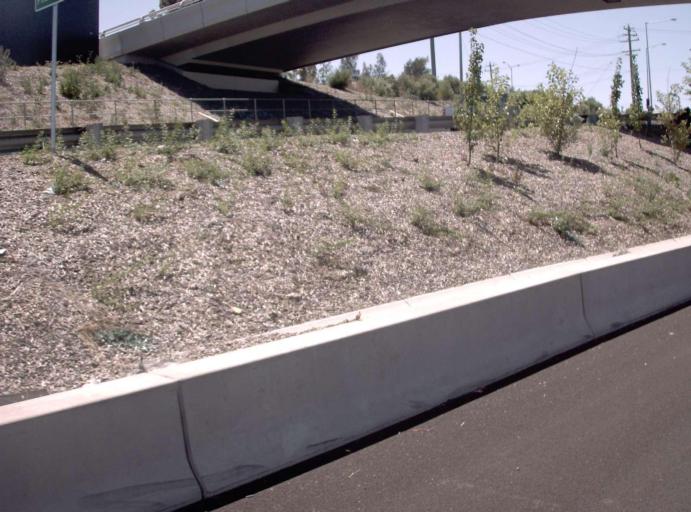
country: AU
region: Victoria
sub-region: Hume
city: Jacana
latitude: -37.6940
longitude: 144.9136
